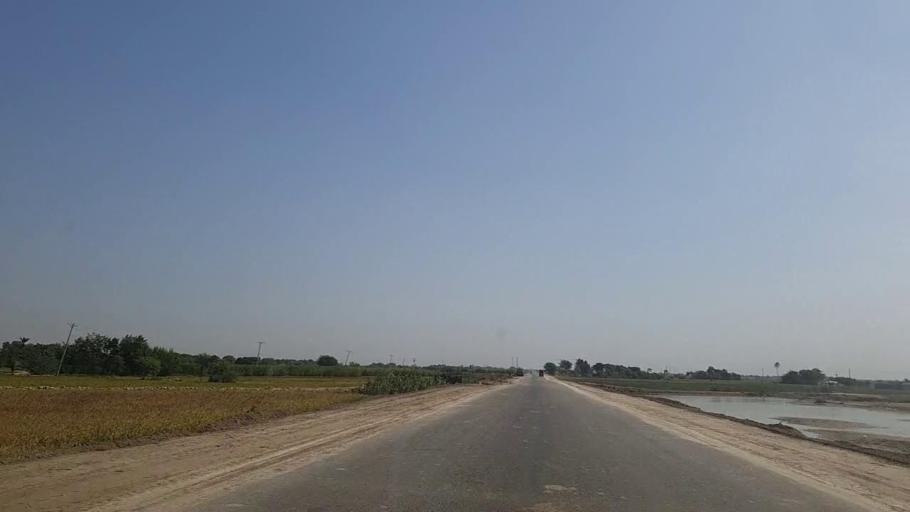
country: PK
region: Sindh
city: Mirpur Batoro
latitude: 24.7523
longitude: 68.2330
